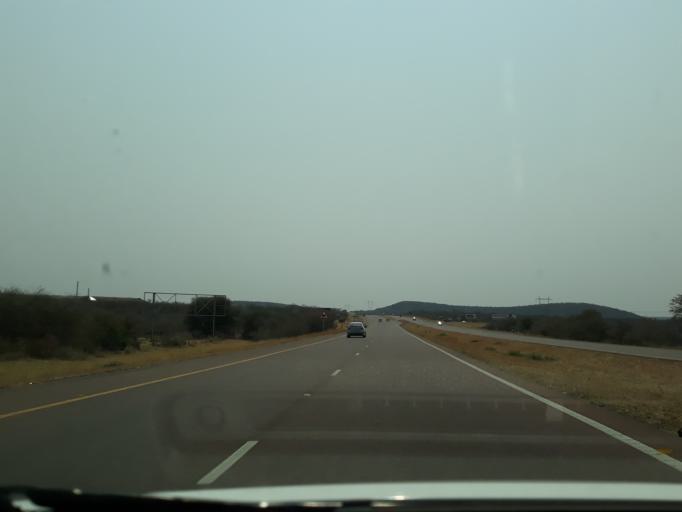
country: BW
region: Kgatleng
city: Bokaa
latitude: -24.4058
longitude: 26.0541
